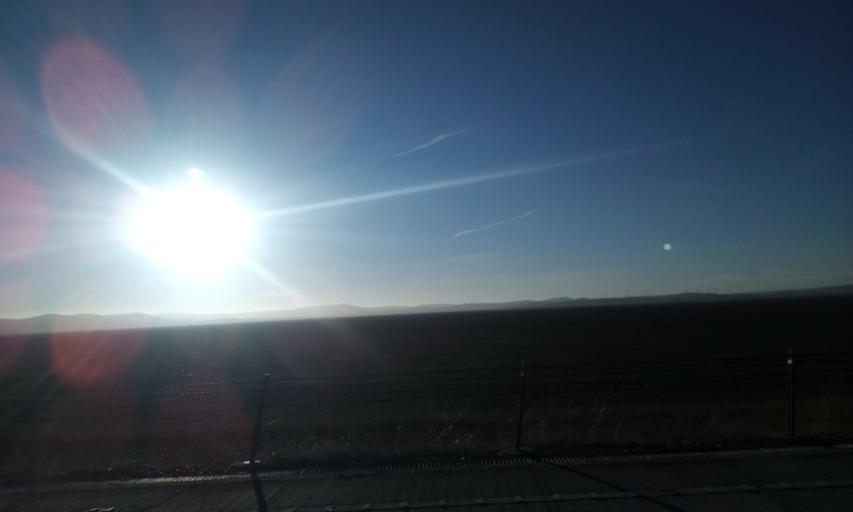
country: AU
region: New South Wales
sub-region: Yass Valley
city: Gundaroo
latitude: -35.0694
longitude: 149.3739
